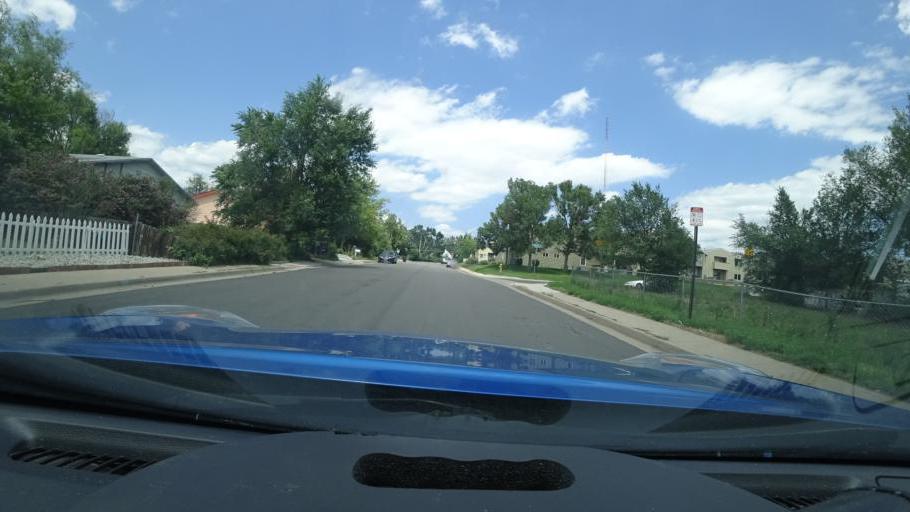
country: US
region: Colorado
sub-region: Arapahoe County
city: Sheridan
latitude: 39.6811
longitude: -105.0087
